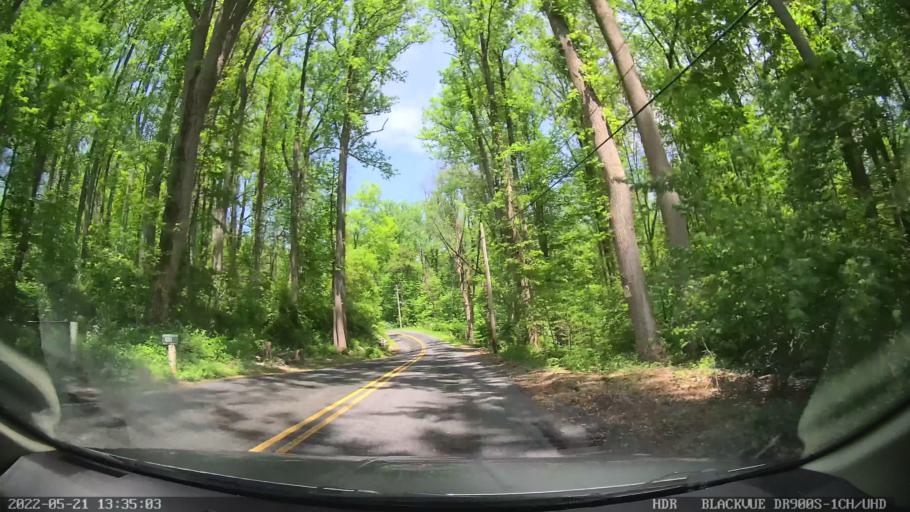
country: US
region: Pennsylvania
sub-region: Berks County
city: Topton
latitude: 40.4464
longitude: -75.6782
